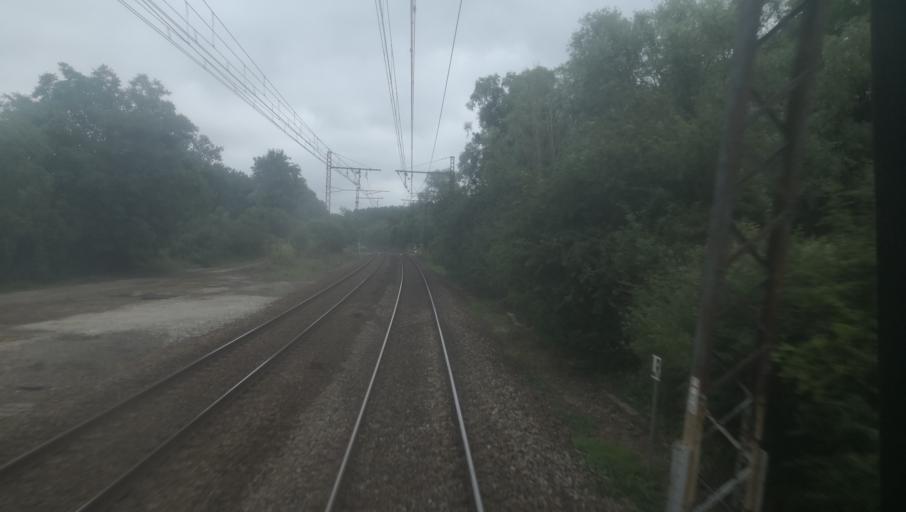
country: FR
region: Centre
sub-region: Departement de l'Indre
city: Reuilly
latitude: 47.1184
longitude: 2.0505
